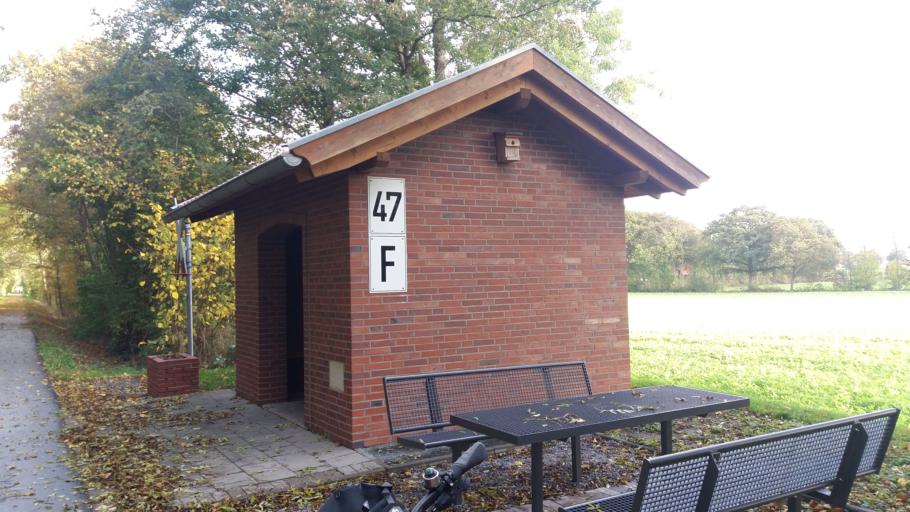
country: DE
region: North Rhine-Westphalia
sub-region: Regierungsbezirk Munster
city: Horstmar
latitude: 52.1047
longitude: 7.3337
